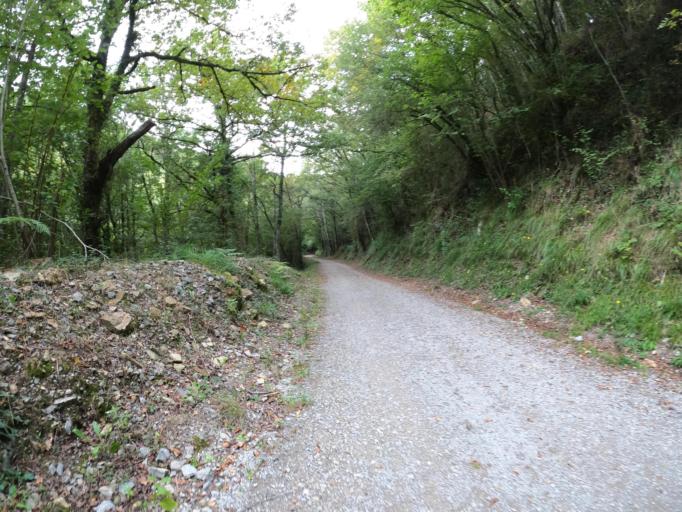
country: ES
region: Navarre
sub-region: Provincia de Navarra
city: Lekunberri
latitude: 42.9820
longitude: -1.8639
